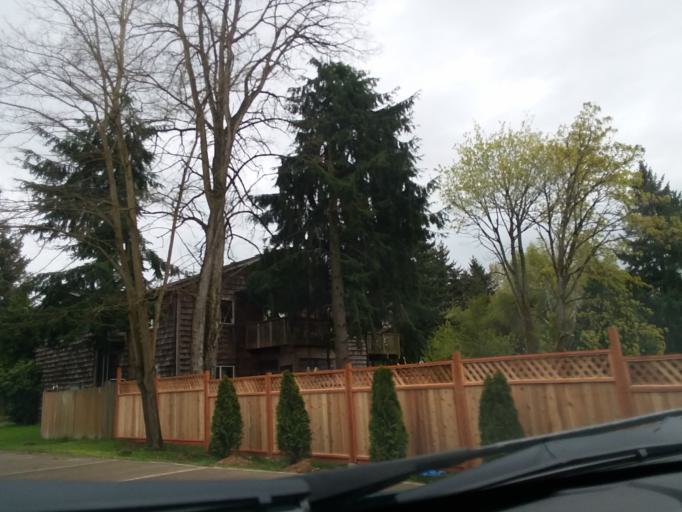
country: US
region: Washington
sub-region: King County
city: Boulevard Park
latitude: 47.4884
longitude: -122.3282
